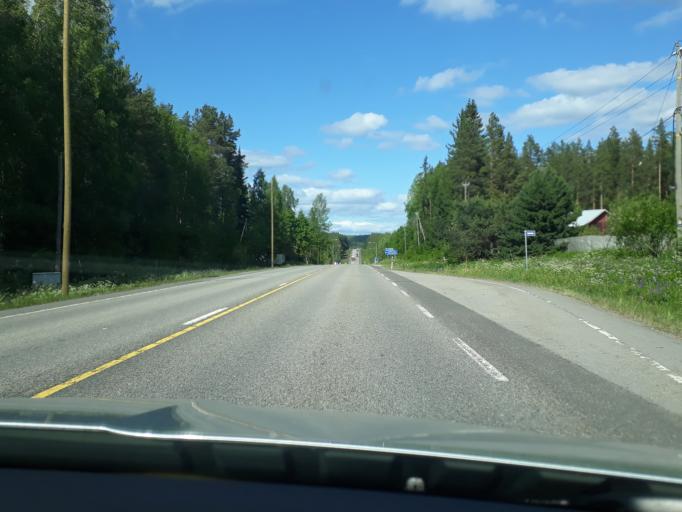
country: FI
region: Central Finland
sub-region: AEaenekoski
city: AEaenekoski
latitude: 62.6554
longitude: 25.7247
